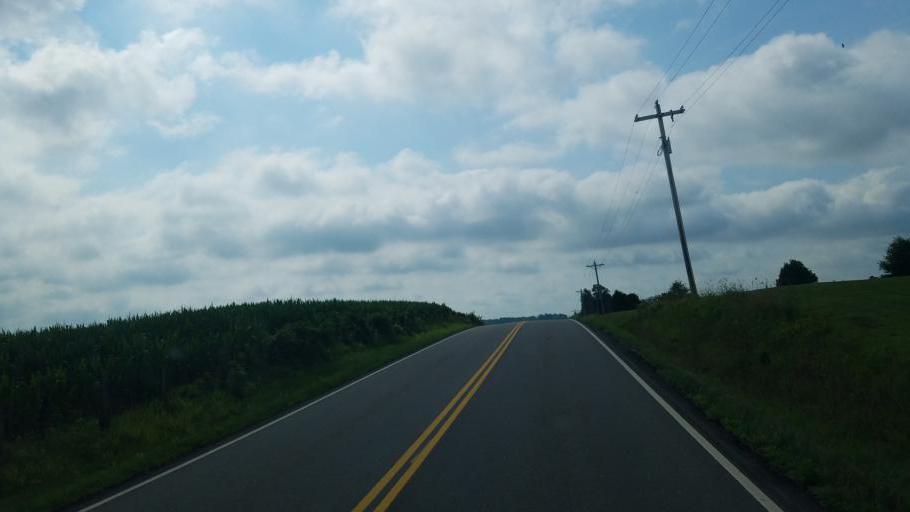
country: US
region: Ohio
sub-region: Licking County
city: Utica
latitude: 40.2222
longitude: -82.5551
